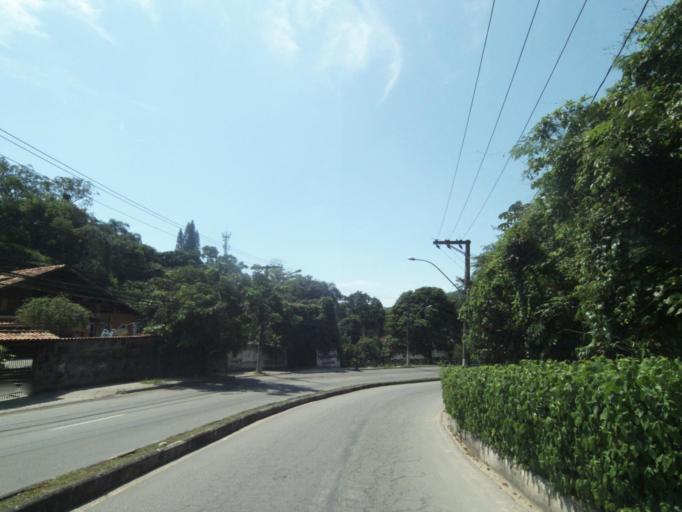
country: BR
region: Rio de Janeiro
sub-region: Niteroi
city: Niteroi
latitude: -22.9037
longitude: -43.0492
